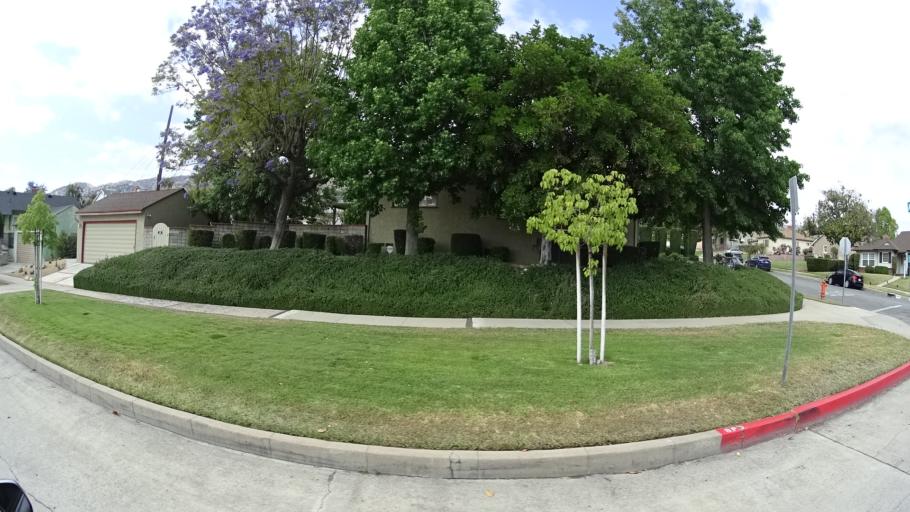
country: US
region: California
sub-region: Los Angeles County
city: Burbank
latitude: 34.1948
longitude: -118.3163
